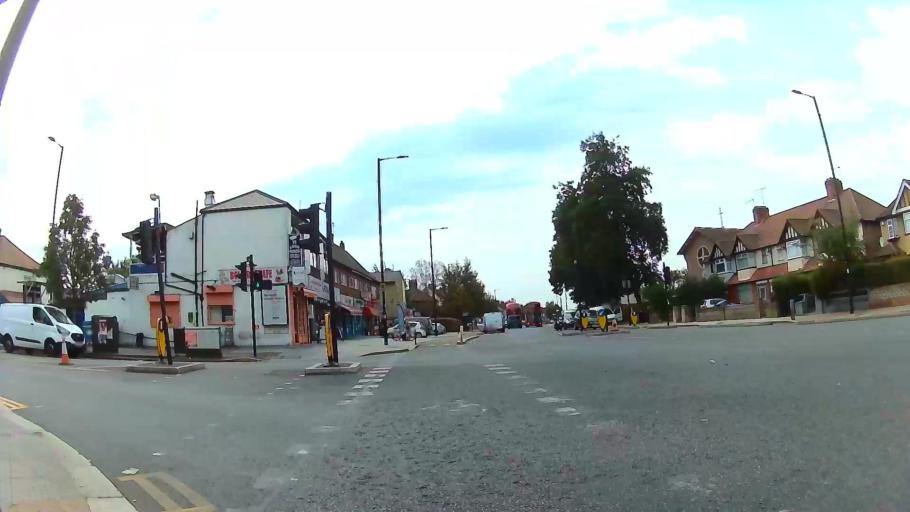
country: GB
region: England
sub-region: Greater London
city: Enfield
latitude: 51.6393
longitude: -0.0479
